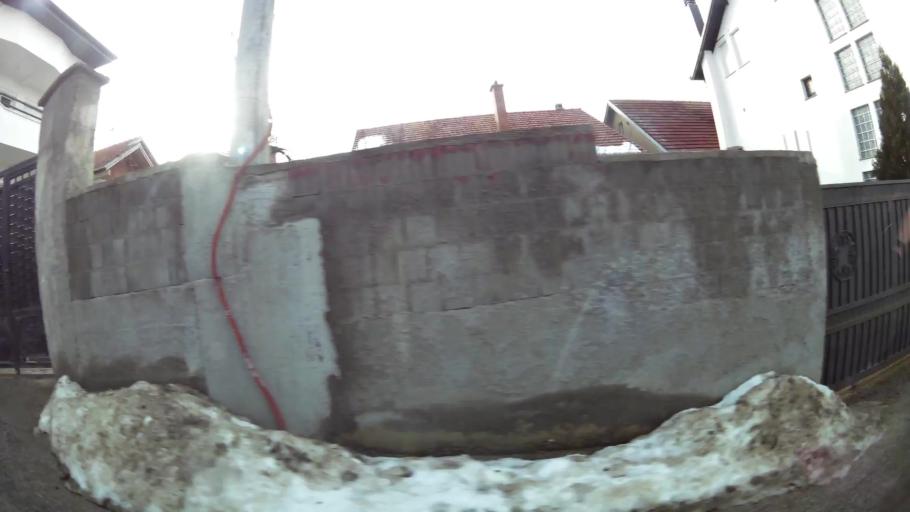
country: XK
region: Pristina
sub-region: Komuna e Prishtines
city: Pristina
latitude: 42.6699
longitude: 21.1809
